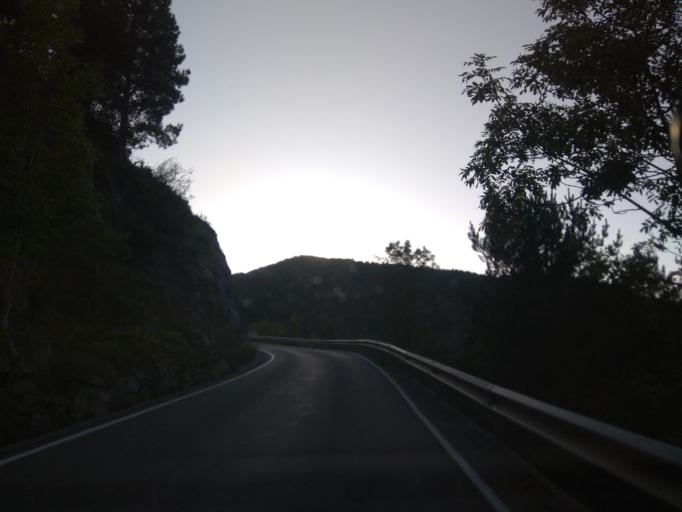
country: ES
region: Catalonia
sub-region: Provincia de Lleida
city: Lles de Cerdanya
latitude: 42.3593
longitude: 1.6889
